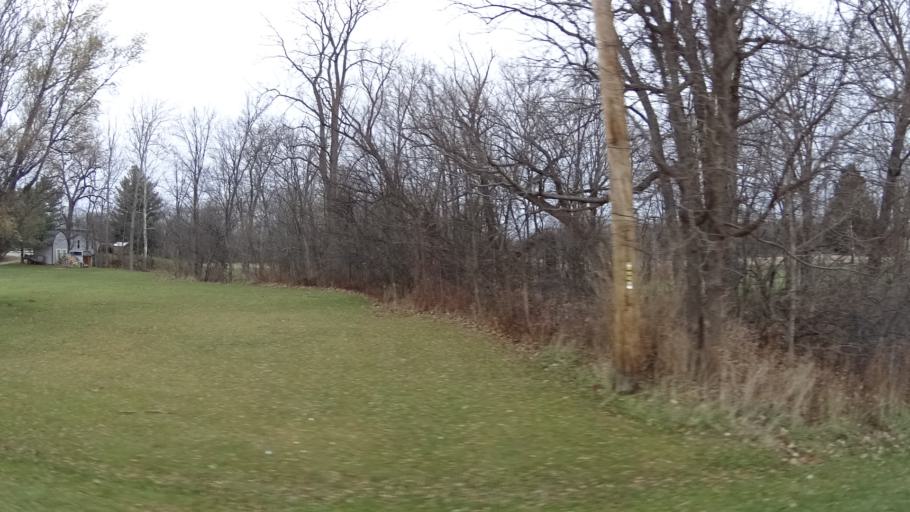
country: US
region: Ohio
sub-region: Lorain County
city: Wellington
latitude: 41.1890
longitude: -82.1790
